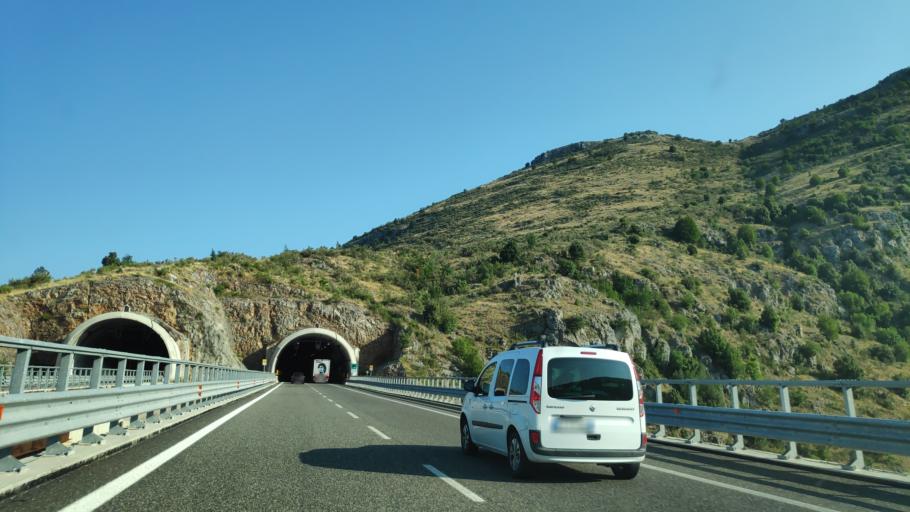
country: IT
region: Basilicate
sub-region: Provincia di Potenza
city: Lauria
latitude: 40.0368
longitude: 15.8733
